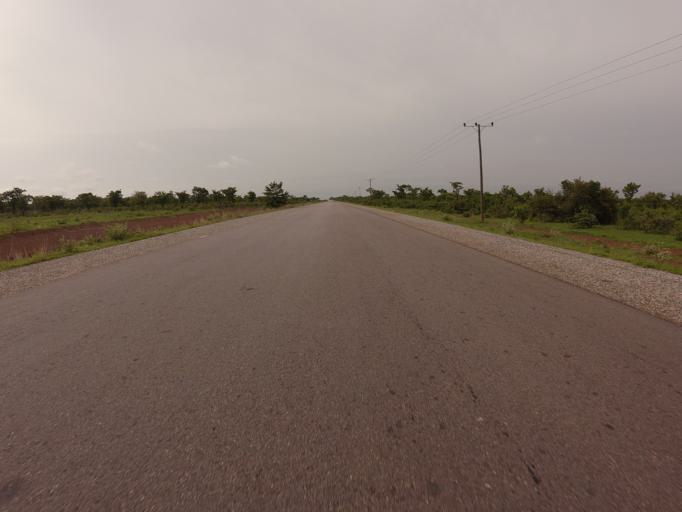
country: GH
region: Northern
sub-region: Yendi
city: Yendi
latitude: 9.6226
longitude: -0.0528
